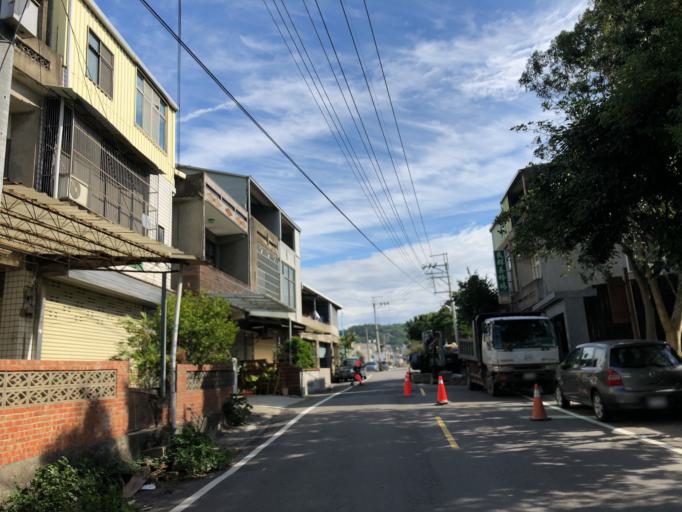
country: TW
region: Taiwan
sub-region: Hsinchu
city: Zhubei
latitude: 24.7909
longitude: 121.0637
